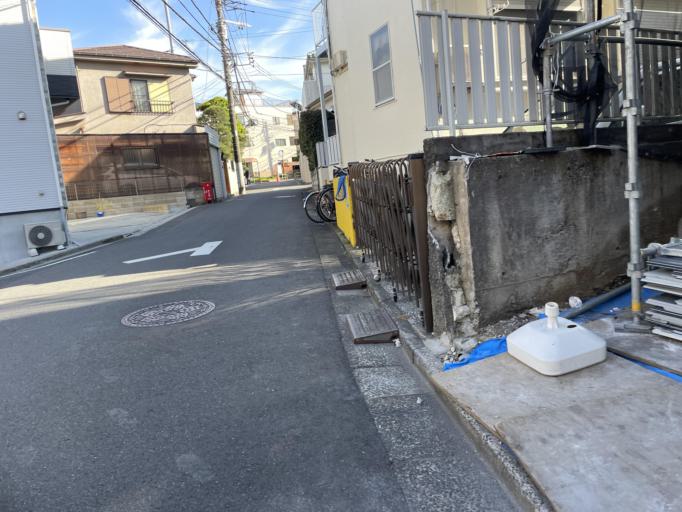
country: JP
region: Tokyo
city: Musashino
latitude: 35.7486
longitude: 139.5800
